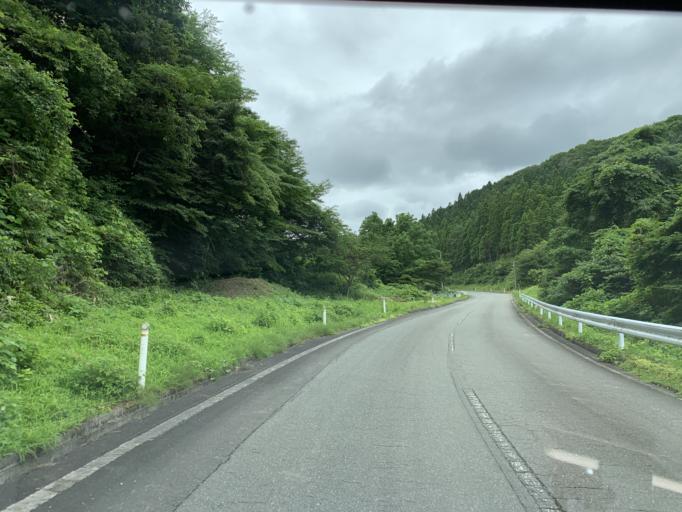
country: JP
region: Iwate
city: Ichinoseki
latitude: 38.8963
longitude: 140.9799
